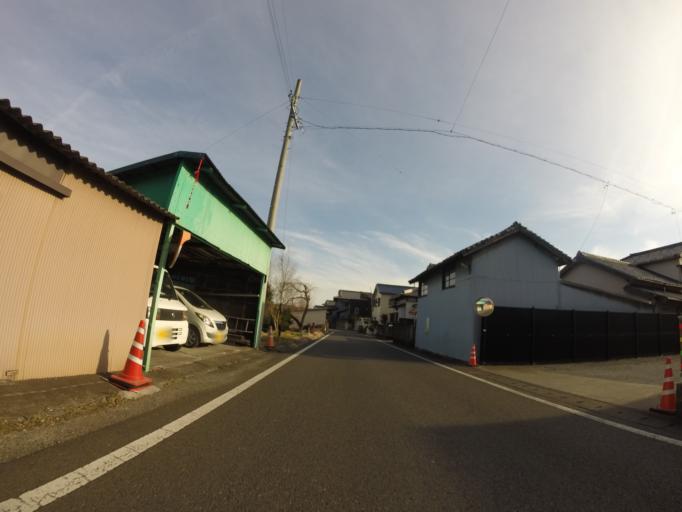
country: JP
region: Shizuoka
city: Shizuoka-shi
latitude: 35.0550
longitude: 138.4741
